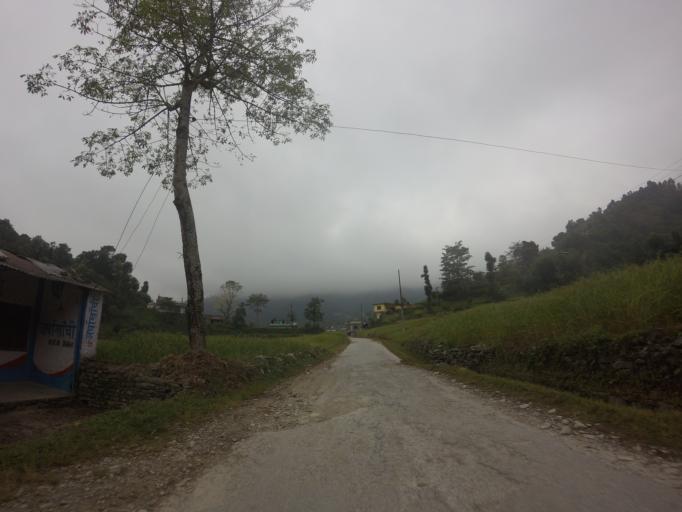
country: NP
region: Western Region
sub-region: Gandaki Zone
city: Pokhara
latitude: 28.2326
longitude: 83.9307
